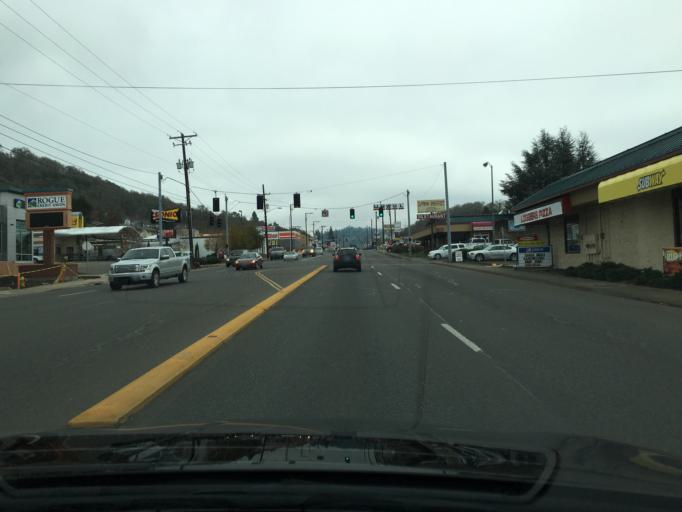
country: US
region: Oregon
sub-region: Douglas County
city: Roseburg
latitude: 43.2261
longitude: -123.3487
